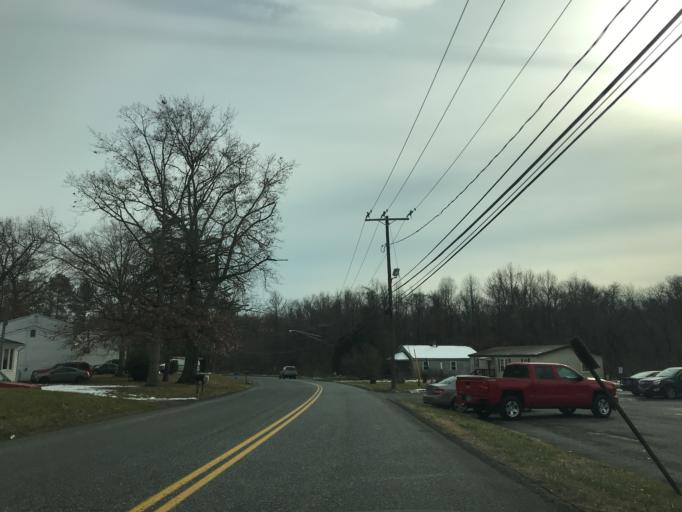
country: US
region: Maryland
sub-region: Harford County
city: Perryman
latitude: 39.4786
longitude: -76.2066
